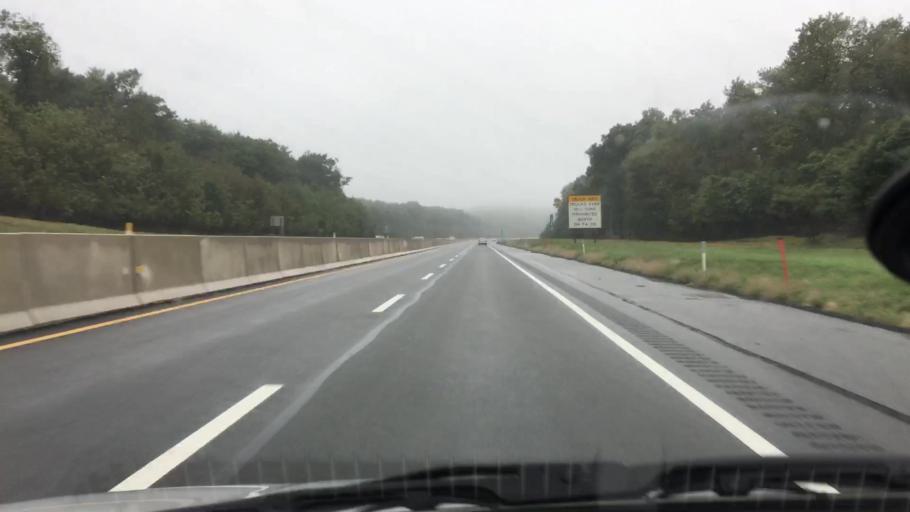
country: US
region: Pennsylvania
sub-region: Luzerne County
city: Mountain Top
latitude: 41.1825
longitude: -75.7871
